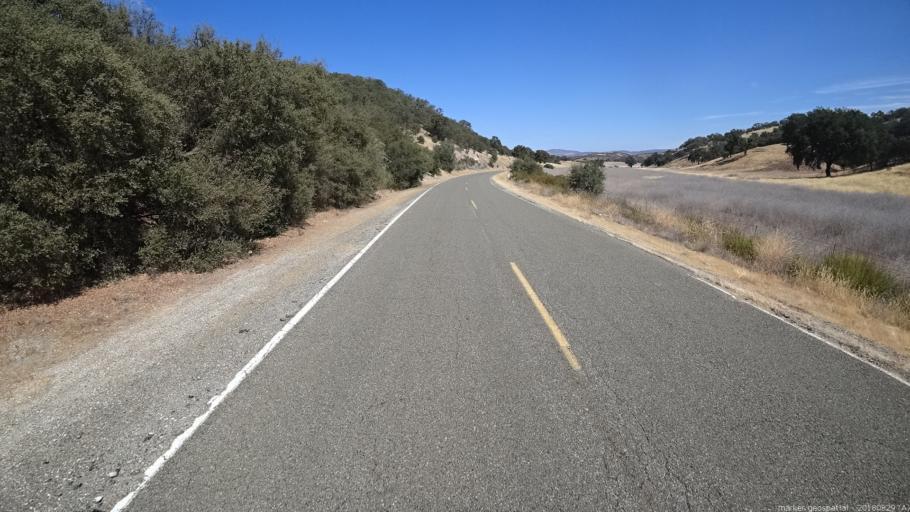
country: US
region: California
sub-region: San Luis Obispo County
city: Lake Nacimiento
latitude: 35.8767
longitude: -121.0658
